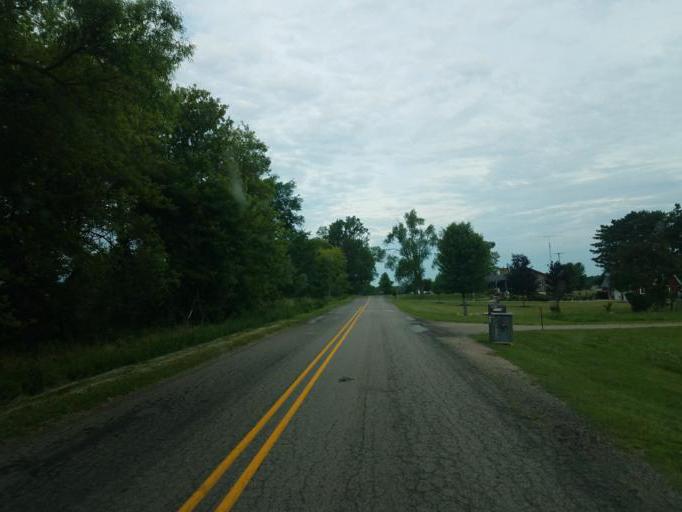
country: US
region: Michigan
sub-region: Barry County
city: Nashville
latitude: 42.6905
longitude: -84.9893
